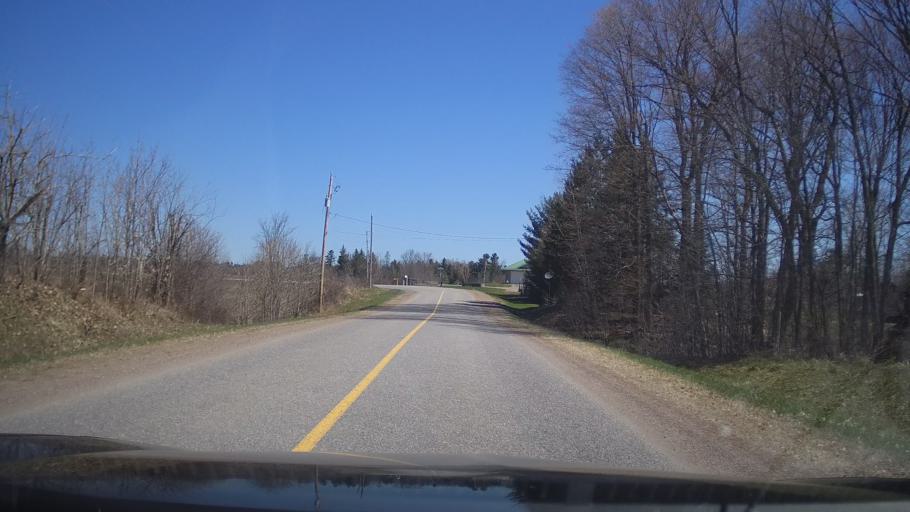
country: CA
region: Ontario
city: Arnprior
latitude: 45.5355
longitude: -76.3917
